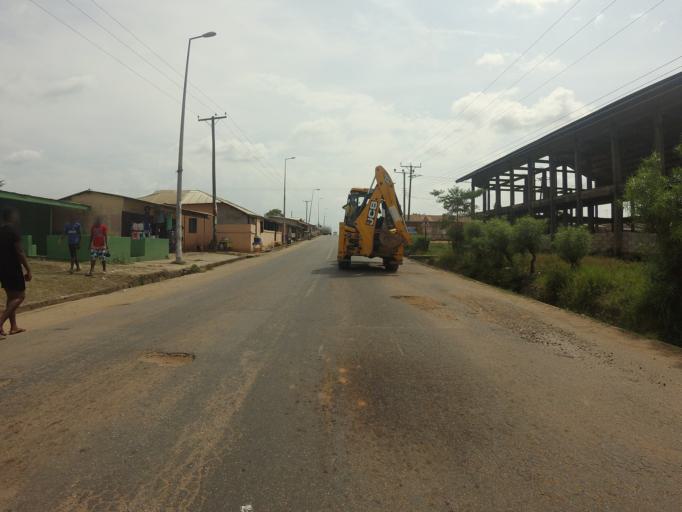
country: GH
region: Eastern
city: Koforidua
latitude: 6.0388
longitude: -0.2600
